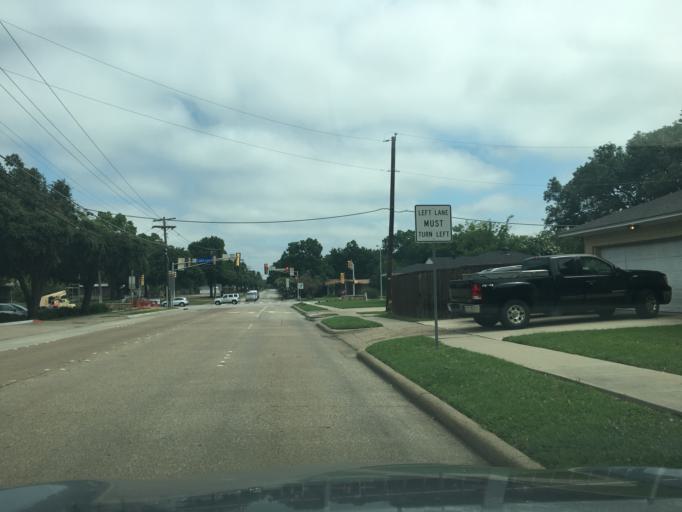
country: US
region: Texas
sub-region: Dallas County
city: Richardson
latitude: 32.9500
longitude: -96.7439
